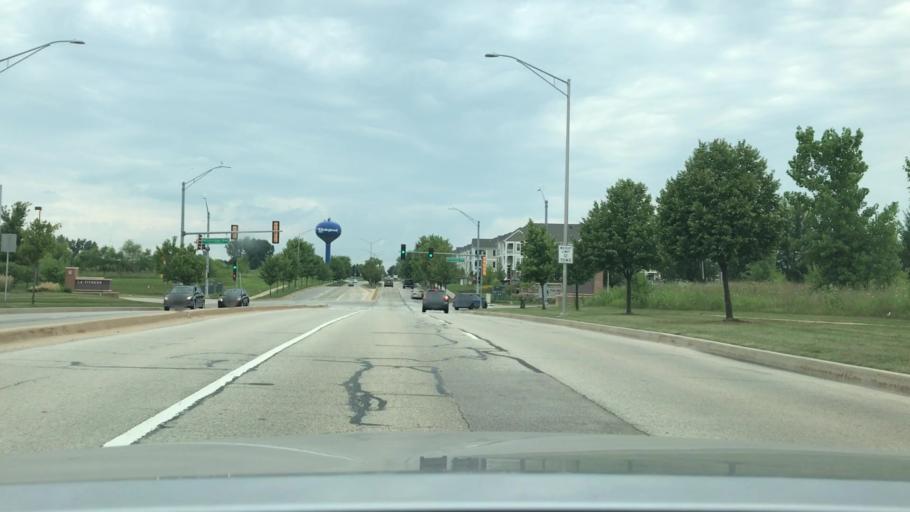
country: US
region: Illinois
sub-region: Will County
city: Bolingbrook
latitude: 41.7143
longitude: -88.0396
